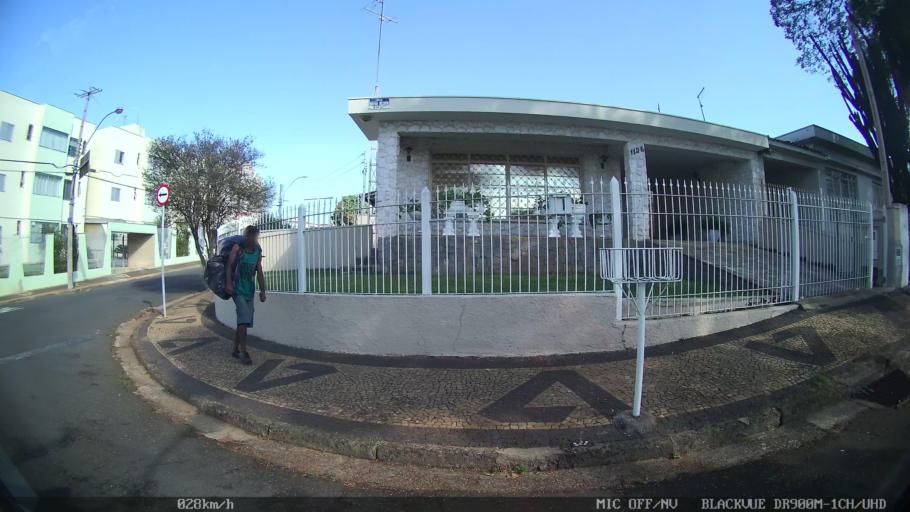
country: BR
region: Sao Paulo
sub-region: Americana
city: Americana
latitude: -22.7522
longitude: -47.3254
